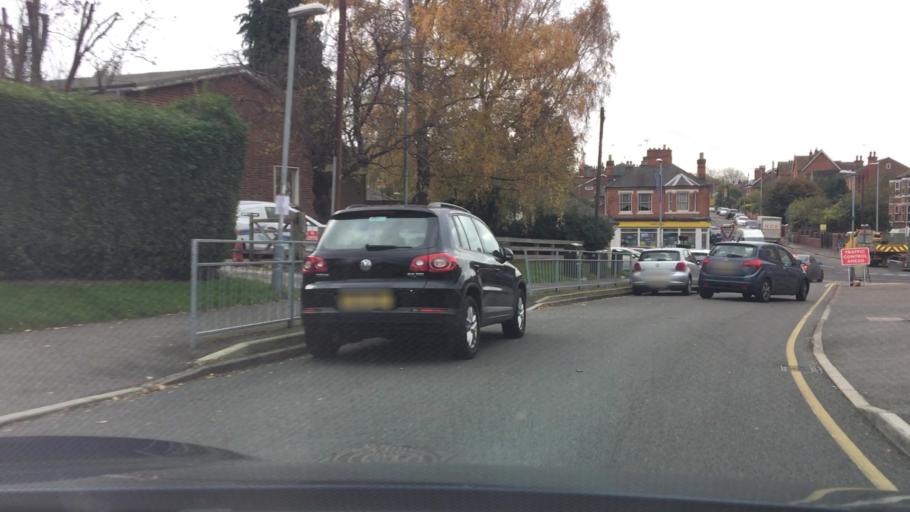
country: GB
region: England
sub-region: Nottinghamshire
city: Radcliffe on Trent
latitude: 52.9477
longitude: -1.0372
